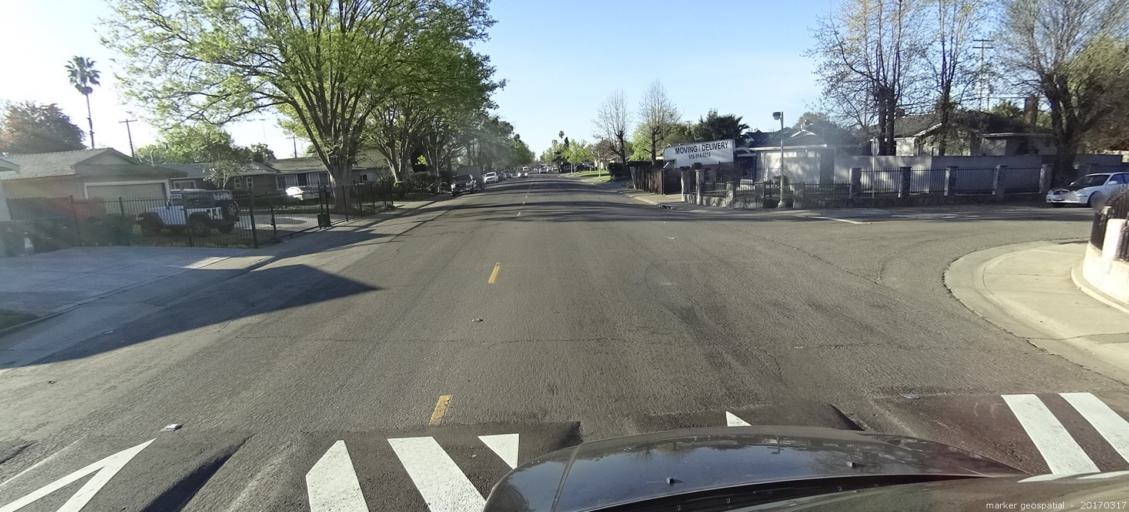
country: US
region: California
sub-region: Sacramento County
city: Parkway
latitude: 38.4921
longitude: -121.4920
